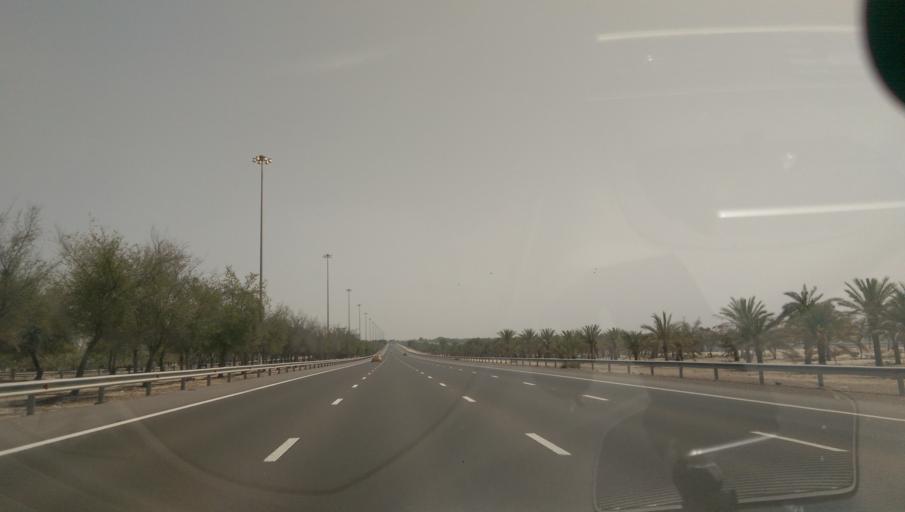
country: AE
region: Abu Dhabi
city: Abu Dhabi
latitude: 24.5034
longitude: 54.6832
